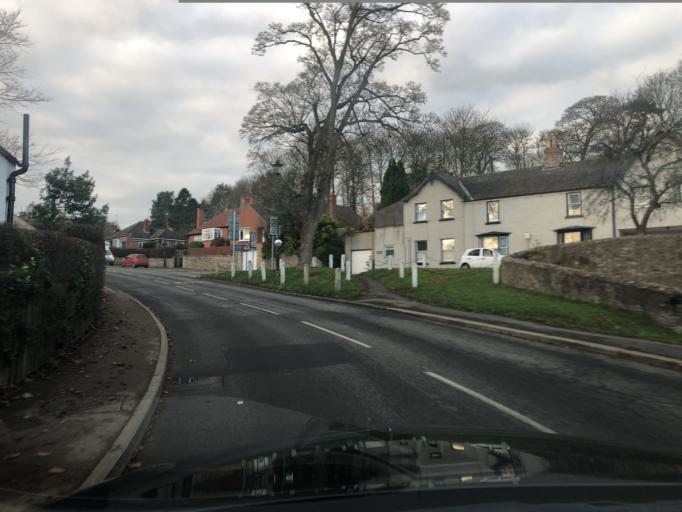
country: GB
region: England
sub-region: North Yorkshire
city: Bedale
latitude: 54.2872
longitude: -1.5952
